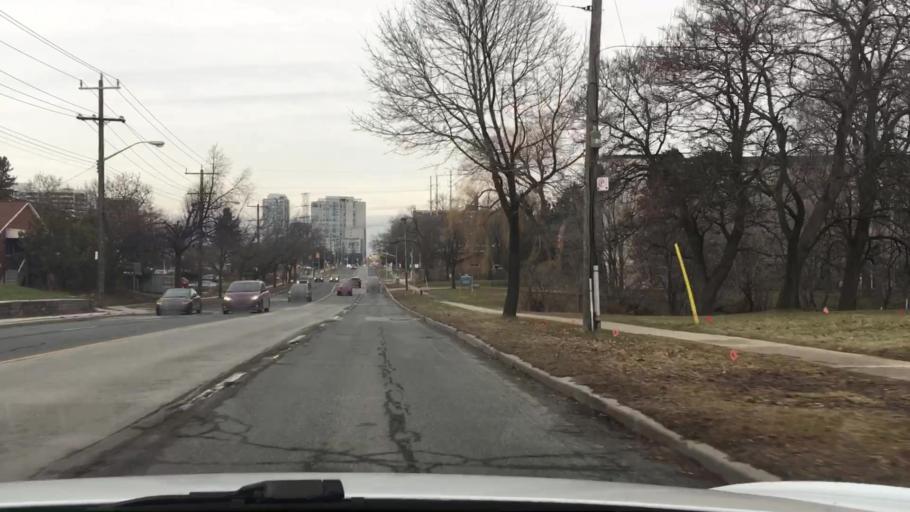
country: CA
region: Ontario
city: Scarborough
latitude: 43.7447
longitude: -79.2623
